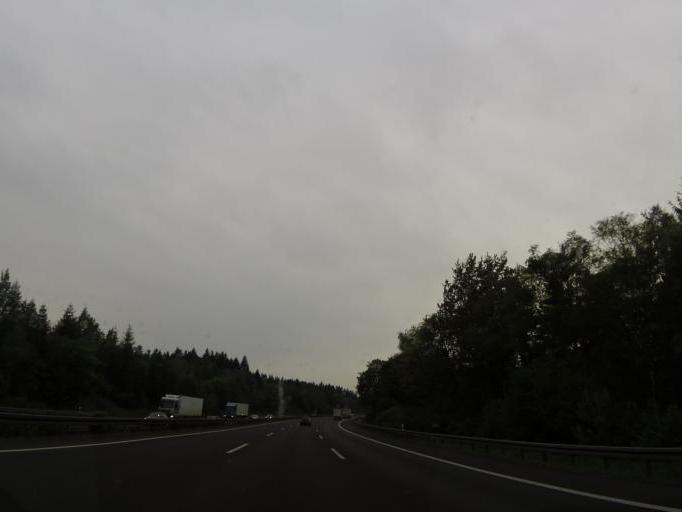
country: DE
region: Lower Saxony
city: Hannoversch Munden
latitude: 51.3747
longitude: 9.6530
